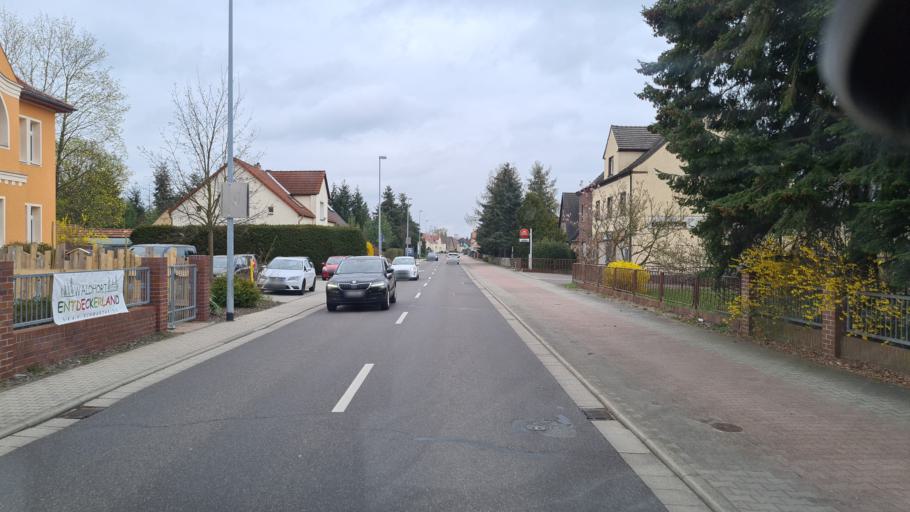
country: DE
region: Brandenburg
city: Schwarzheide
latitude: 51.4897
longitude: 13.8269
